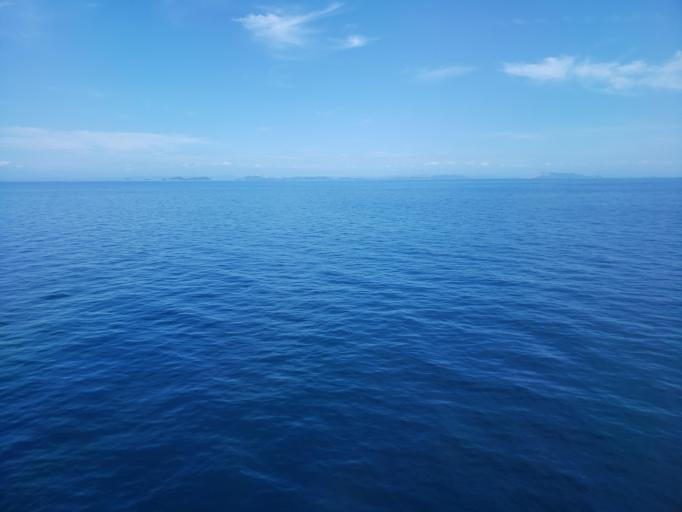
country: JP
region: Hyogo
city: Fukura
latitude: 34.4935
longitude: 134.5683
